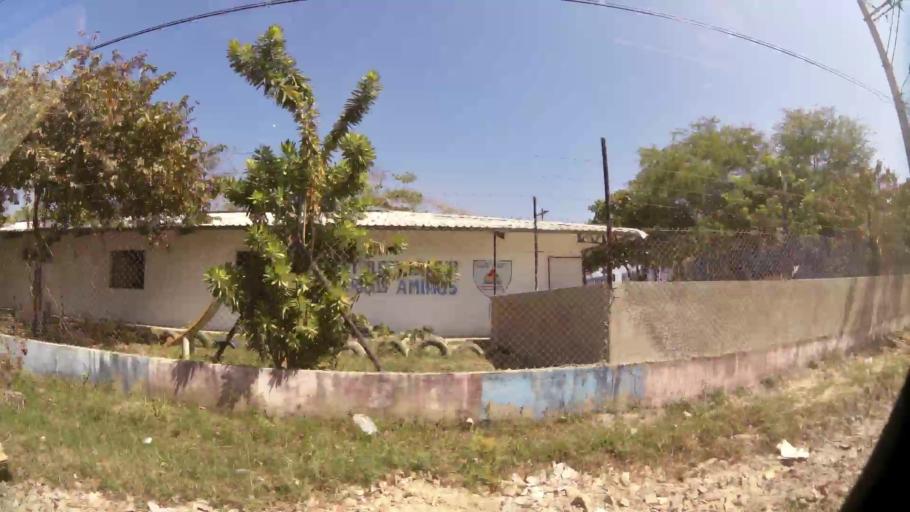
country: CO
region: Bolivar
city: Cartagena
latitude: 10.3854
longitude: -75.4537
